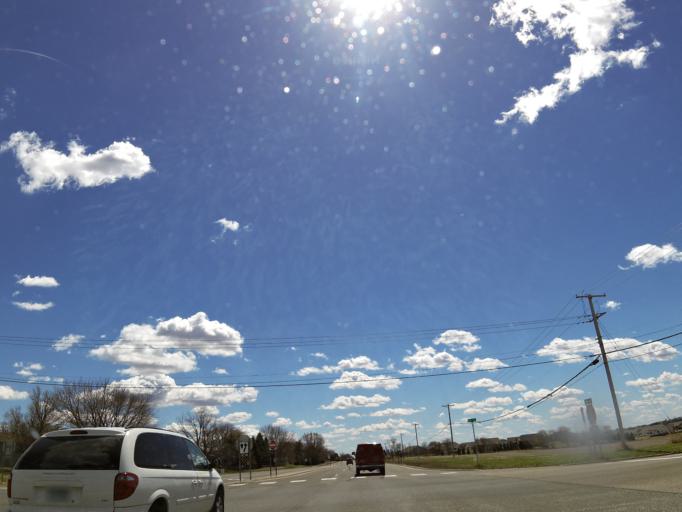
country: US
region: Minnesota
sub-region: Washington County
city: Cottage Grove
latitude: 44.8554
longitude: -92.9490
